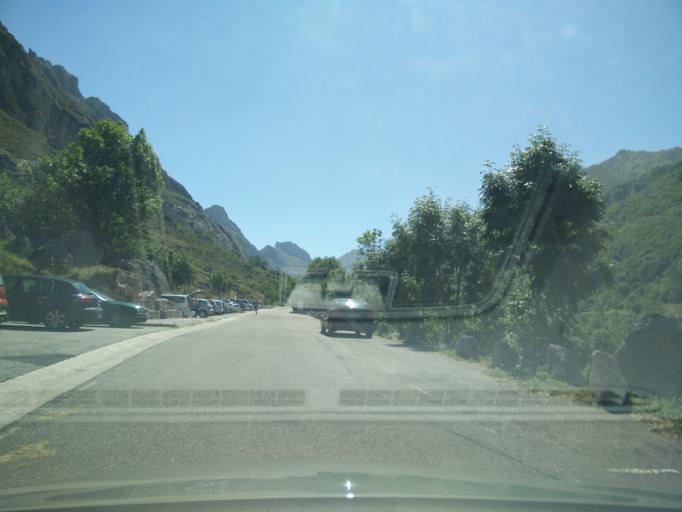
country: ES
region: Asturias
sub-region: Province of Asturias
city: Pola de Somiedo
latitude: 43.0705
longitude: -6.1950
